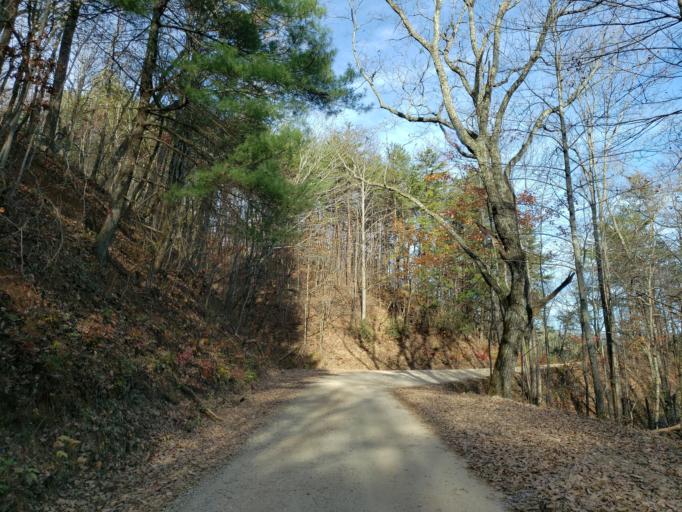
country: US
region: Georgia
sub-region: Lumpkin County
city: Dahlonega
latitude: 34.6369
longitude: -84.0999
